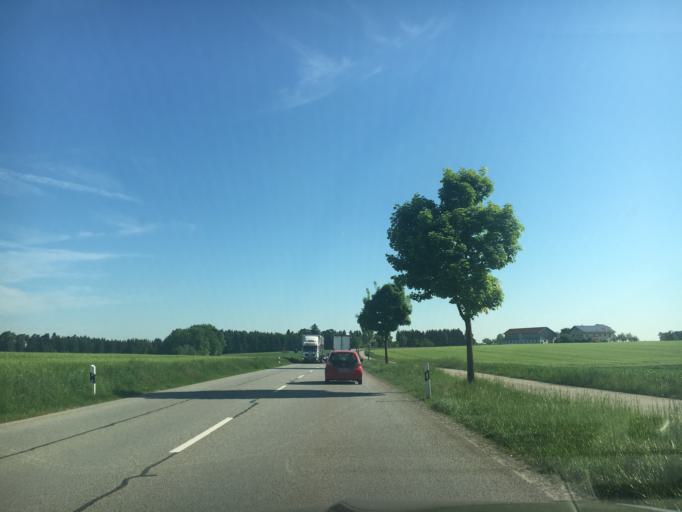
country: DE
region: Bavaria
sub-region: Upper Bavaria
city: Unterneukirchen
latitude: 48.1845
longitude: 12.6335
